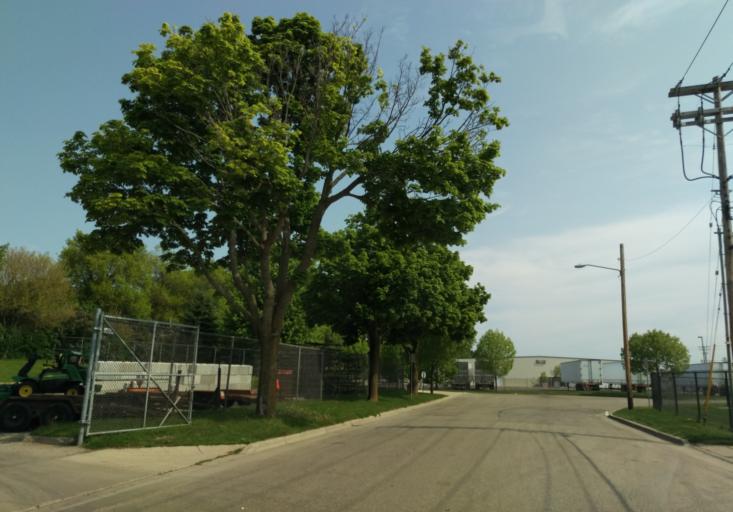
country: US
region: Wisconsin
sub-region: Dane County
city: Shorewood Hills
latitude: 43.0334
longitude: -89.4606
